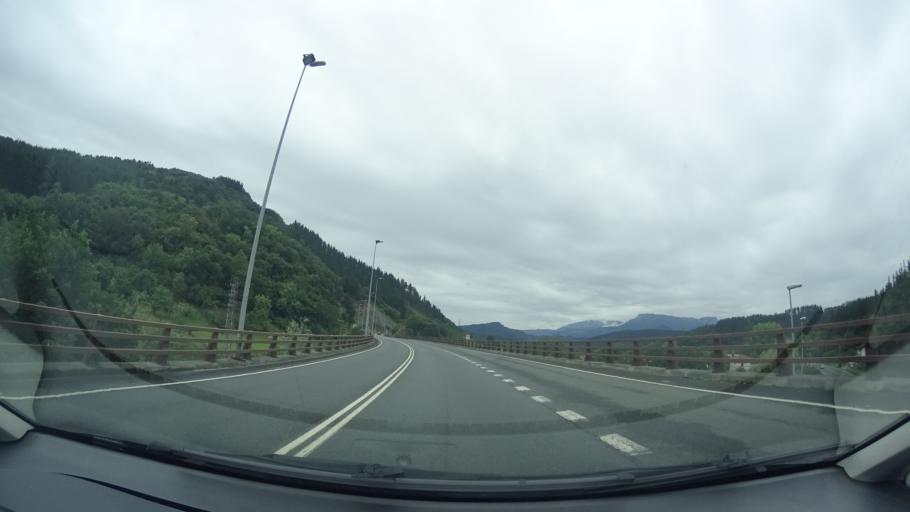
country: ES
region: Basque Country
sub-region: Bizkaia
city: Amorebieta
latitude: 43.1774
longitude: -2.7750
